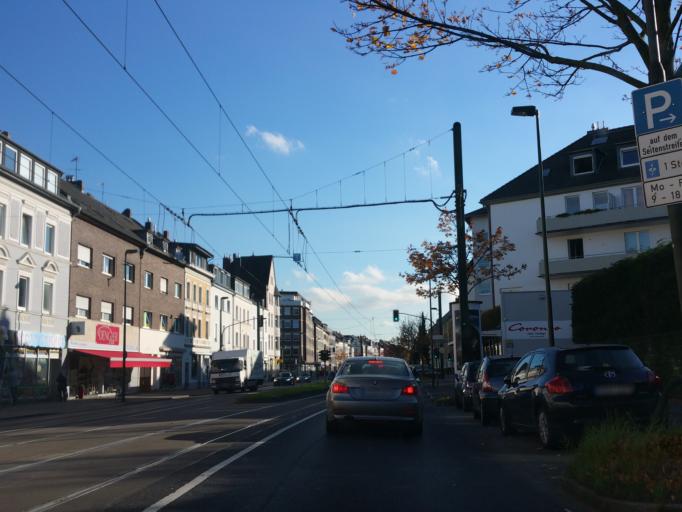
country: DE
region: North Rhine-Westphalia
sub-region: Regierungsbezirk Dusseldorf
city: Dusseldorf
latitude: 51.1902
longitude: 6.8165
